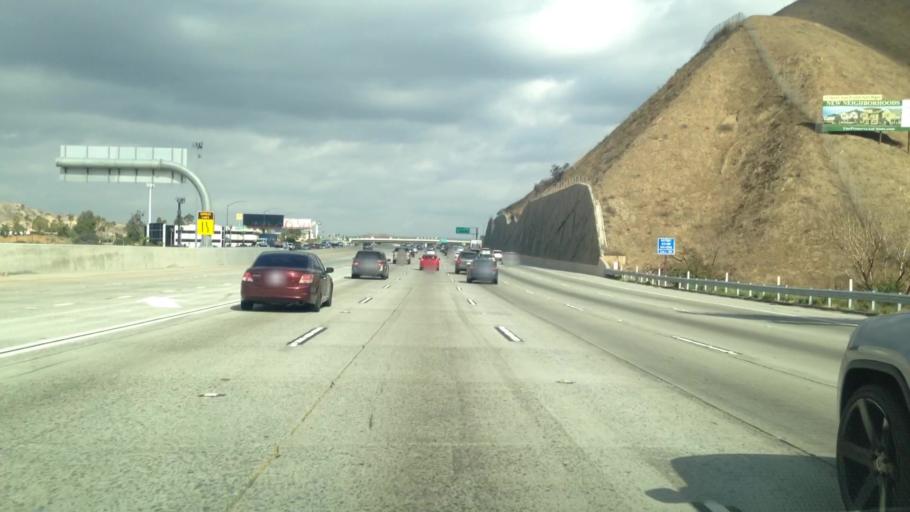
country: US
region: California
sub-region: Riverside County
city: Corona
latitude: 33.8735
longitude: -117.6635
